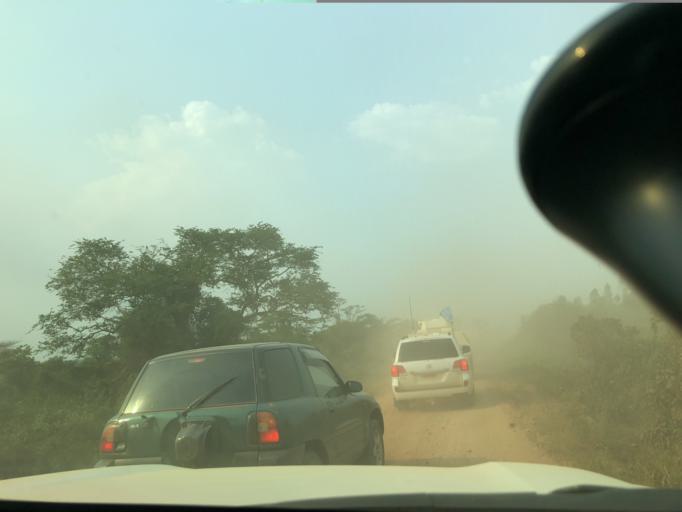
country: CD
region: Nord Kivu
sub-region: North Kivu
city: Butembo
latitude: 0.1105
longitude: 29.6391
